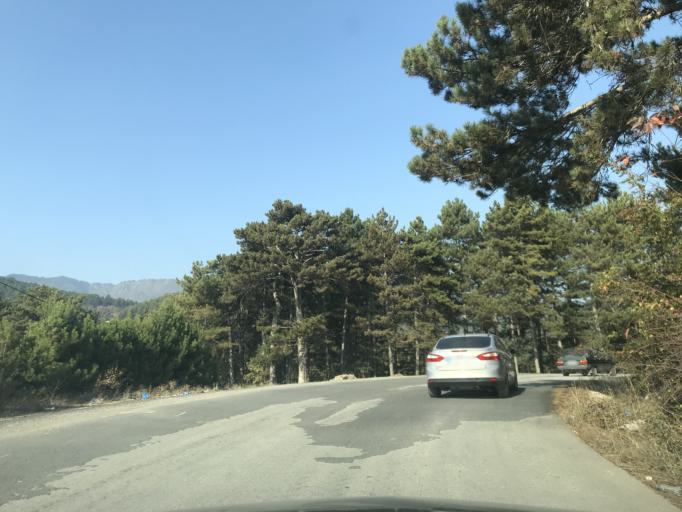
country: TR
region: Bolu
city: Bolu
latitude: 40.7804
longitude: 31.6320
